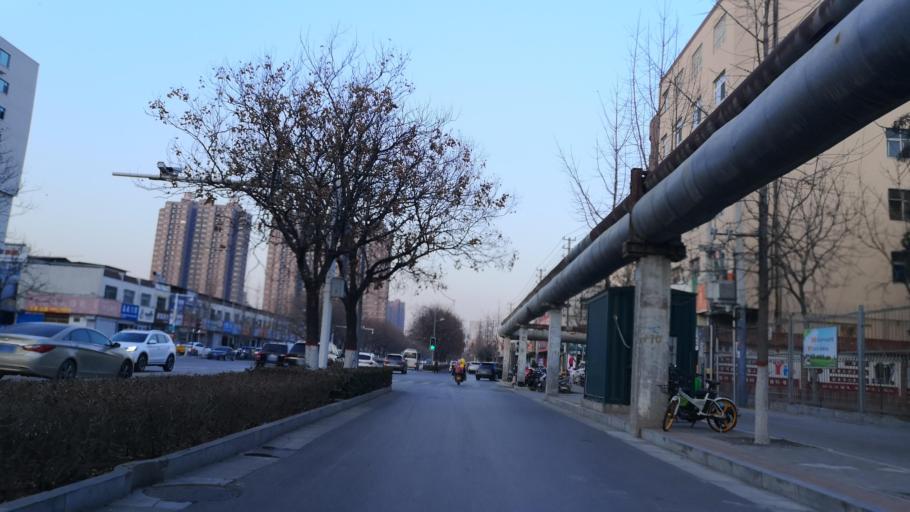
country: CN
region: Henan Sheng
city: Puyang
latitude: 35.7686
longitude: 115.0142
